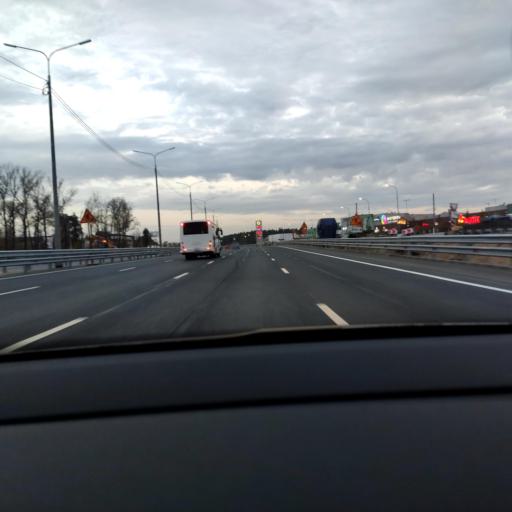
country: RU
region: Moskovskaya
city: Pushkino
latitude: 55.9974
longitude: 37.8776
